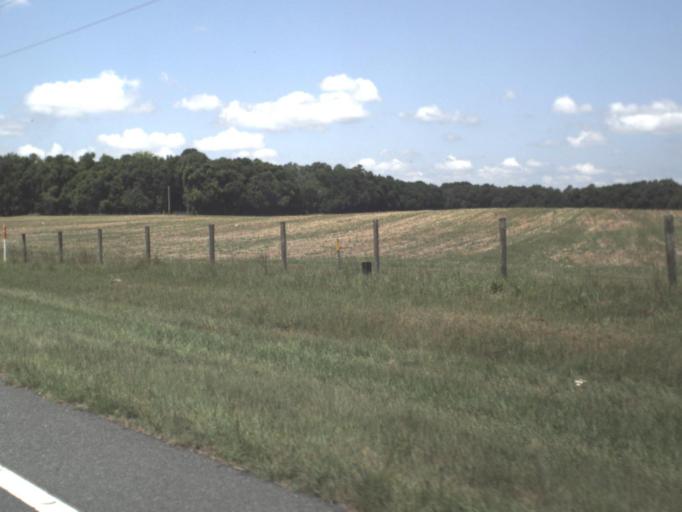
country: US
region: Florida
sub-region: Levy County
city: Williston
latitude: 29.4194
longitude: -82.4268
